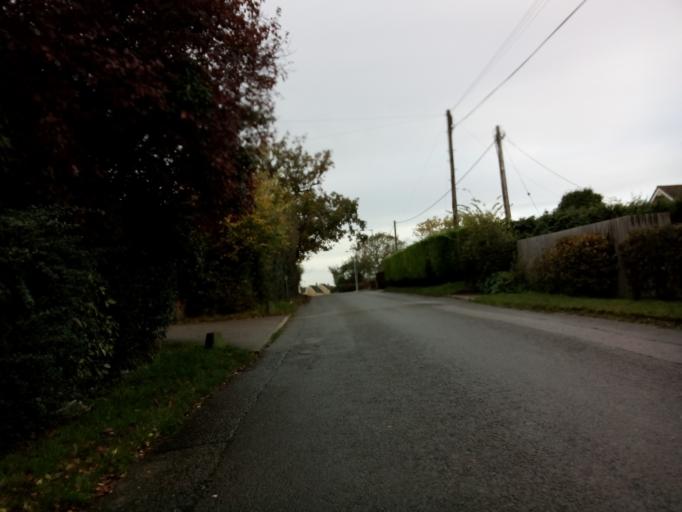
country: GB
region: England
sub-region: Suffolk
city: Stowmarket
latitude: 52.1876
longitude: 1.0175
